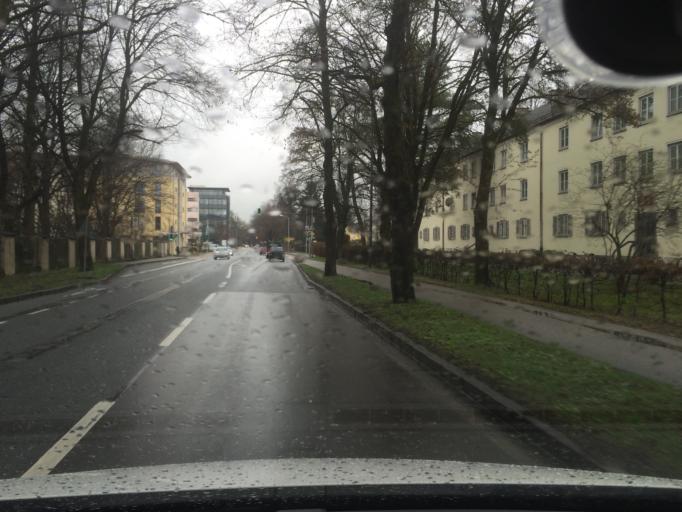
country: DE
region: Bavaria
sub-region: Upper Bavaria
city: Rosenheim
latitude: 47.8677
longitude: 12.1103
